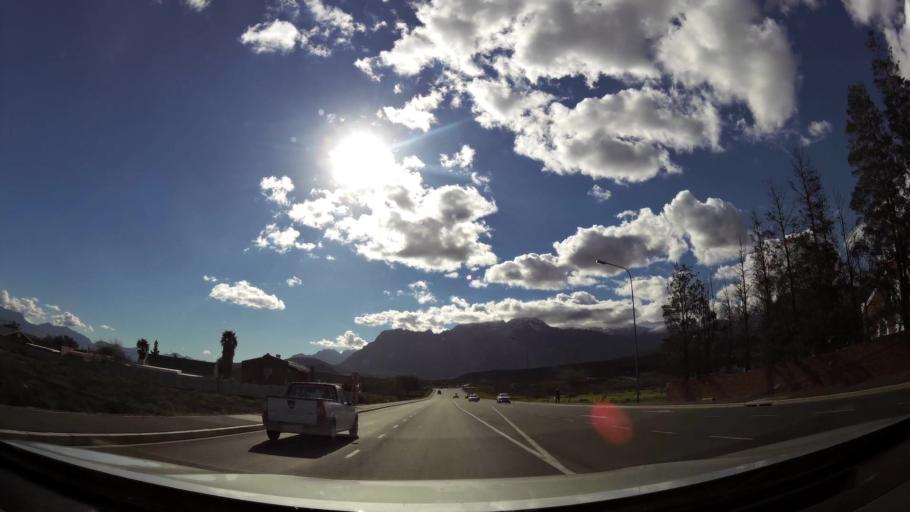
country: ZA
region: Western Cape
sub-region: Cape Winelands District Municipality
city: Worcester
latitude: -33.6374
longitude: 19.4296
